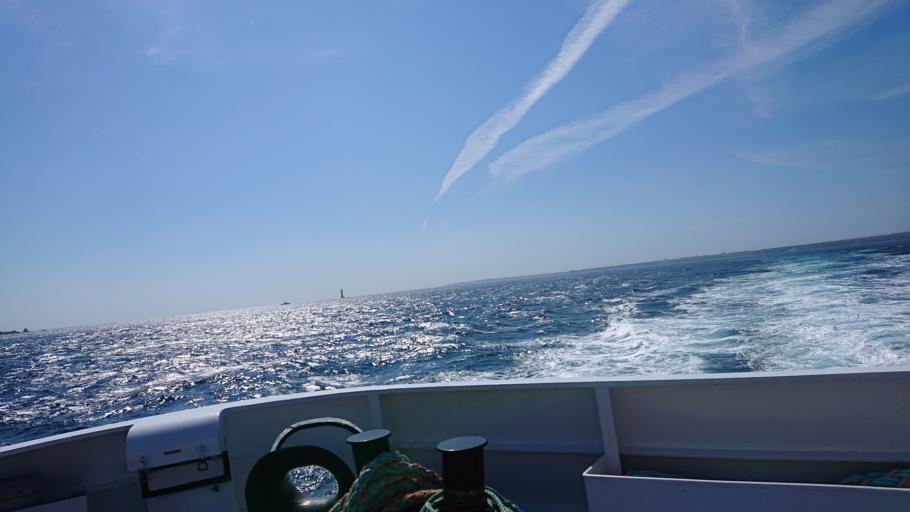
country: FR
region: Brittany
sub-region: Departement du Finistere
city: Lampaul-Plouarzel
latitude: 48.4440
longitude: -4.9895
